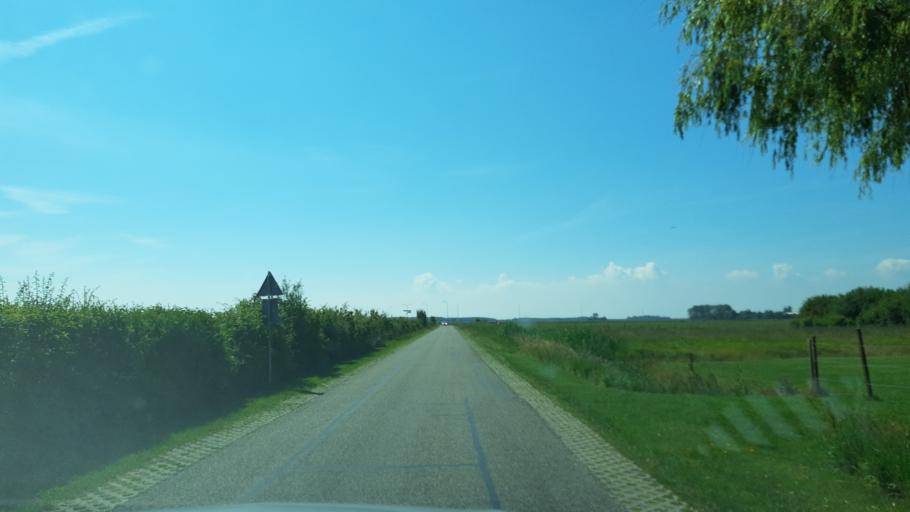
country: NL
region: Zeeland
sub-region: Schouwen-Duiveland
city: Renesse
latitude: 51.7169
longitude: 3.7740
